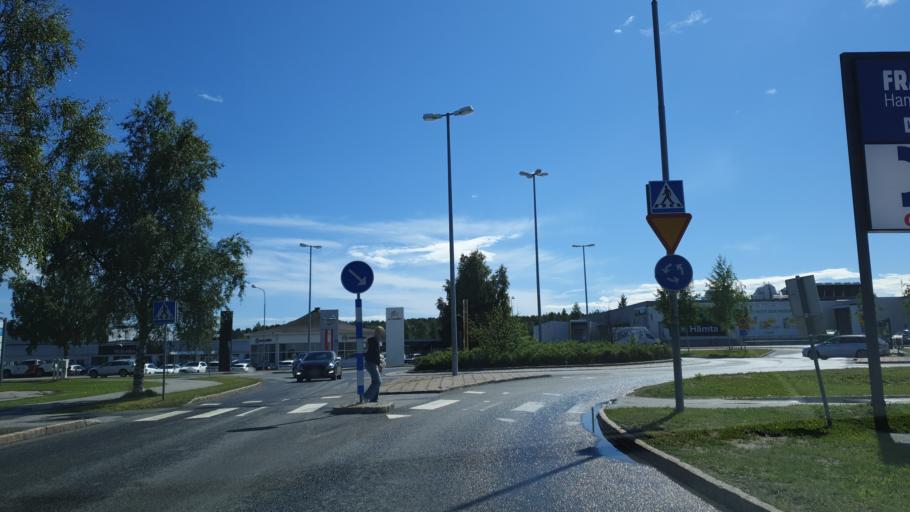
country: SE
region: Vaesterbotten
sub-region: Umea Kommun
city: Ersmark
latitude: 63.8518
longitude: 20.3020
